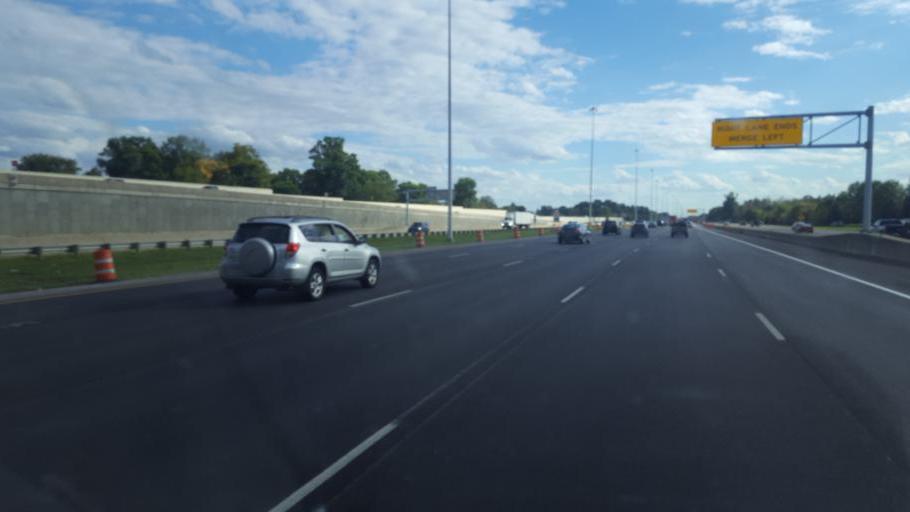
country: US
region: Ohio
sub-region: Franklin County
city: Gahanna
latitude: 40.0480
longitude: -82.9024
